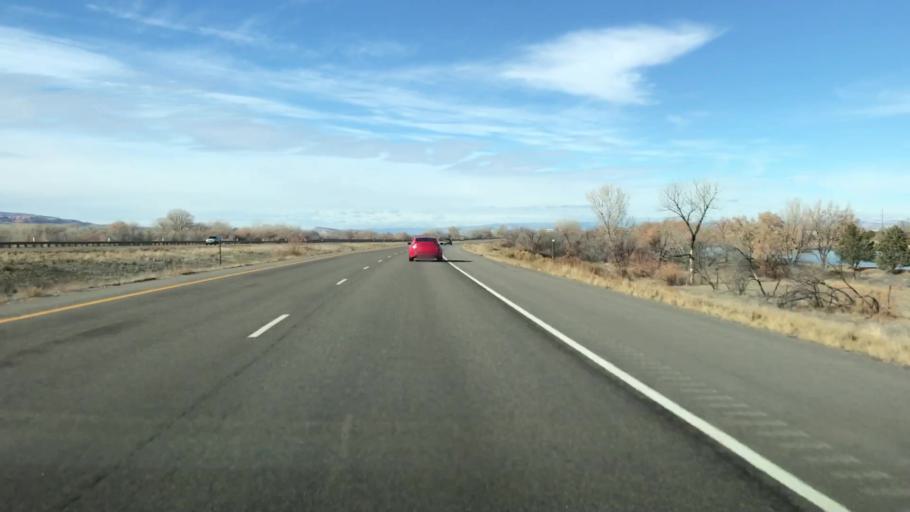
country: US
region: Colorado
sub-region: Mesa County
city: Redlands
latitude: 39.1201
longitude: -108.6736
